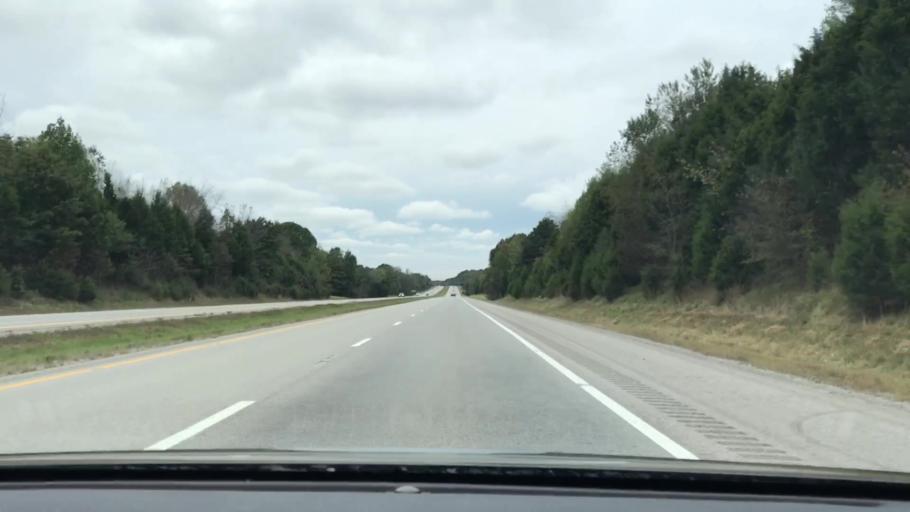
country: US
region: Kentucky
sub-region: Barren County
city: Cave City
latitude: 37.0305
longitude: -86.0500
